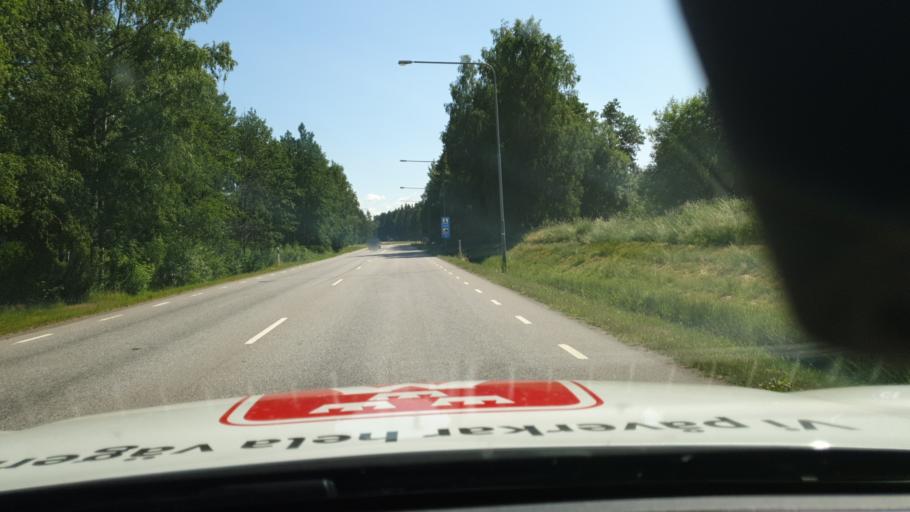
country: SE
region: Vaestra Goetaland
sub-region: Lidkopings Kommun
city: Lidkoping
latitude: 58.5212
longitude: 13.1132
